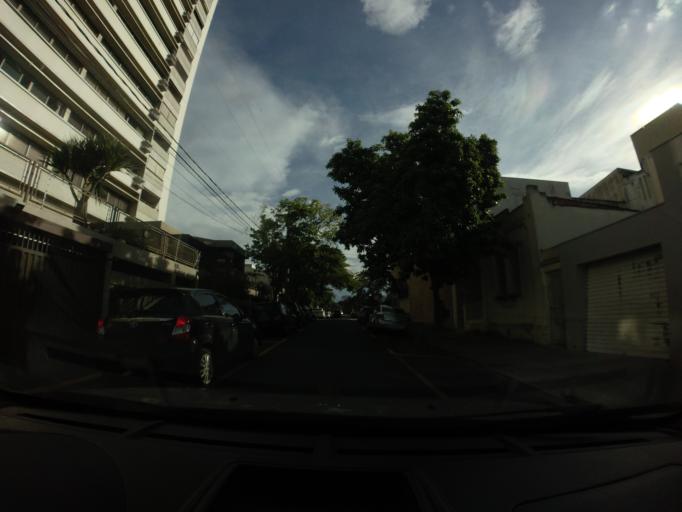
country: BR
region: Sao Paulo
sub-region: Piracicaba
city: Piracicaba
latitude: -22.7279
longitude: -47.6417
